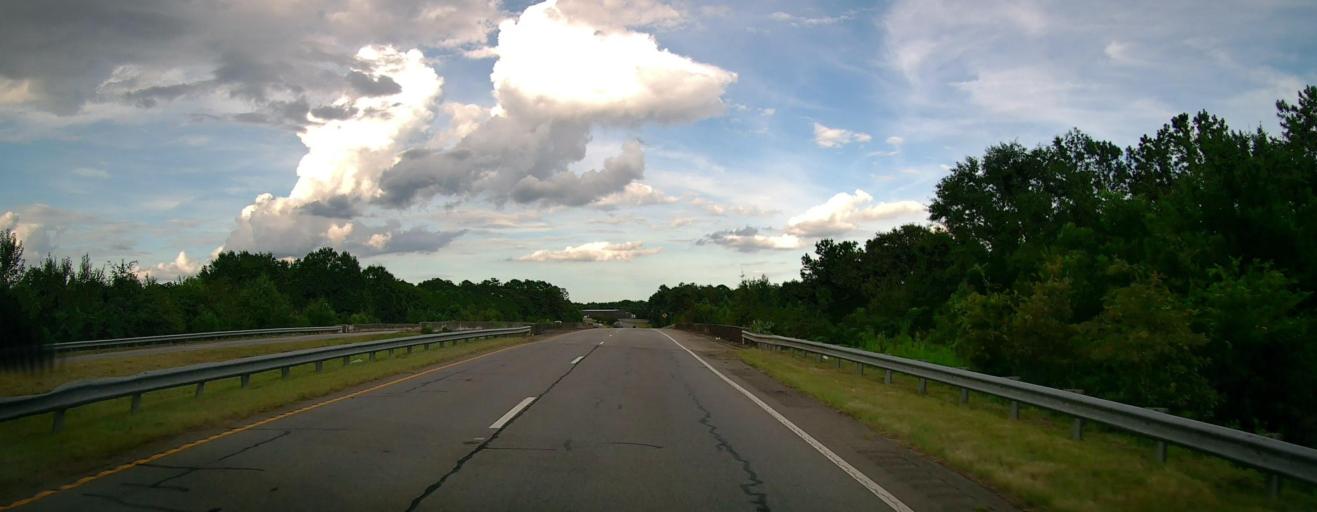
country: US
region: Georgia
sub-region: Peach County
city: Byron
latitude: 32.6357
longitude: -83.7756
